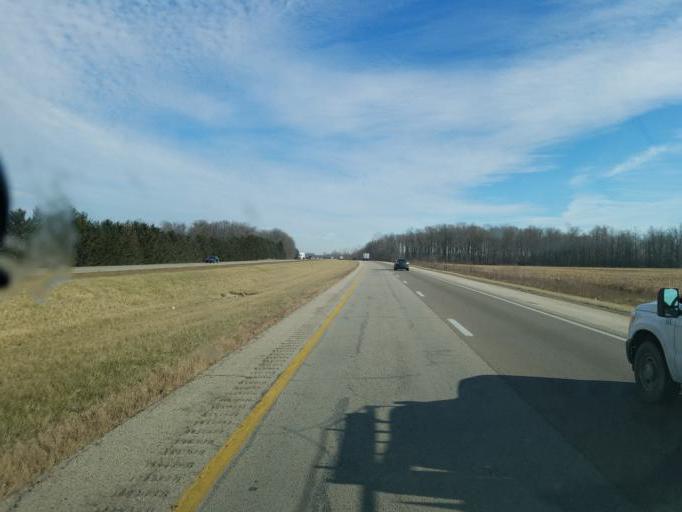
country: US
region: Ohio
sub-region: Preble County
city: New Paris
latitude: 39.8293
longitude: -84.7364
